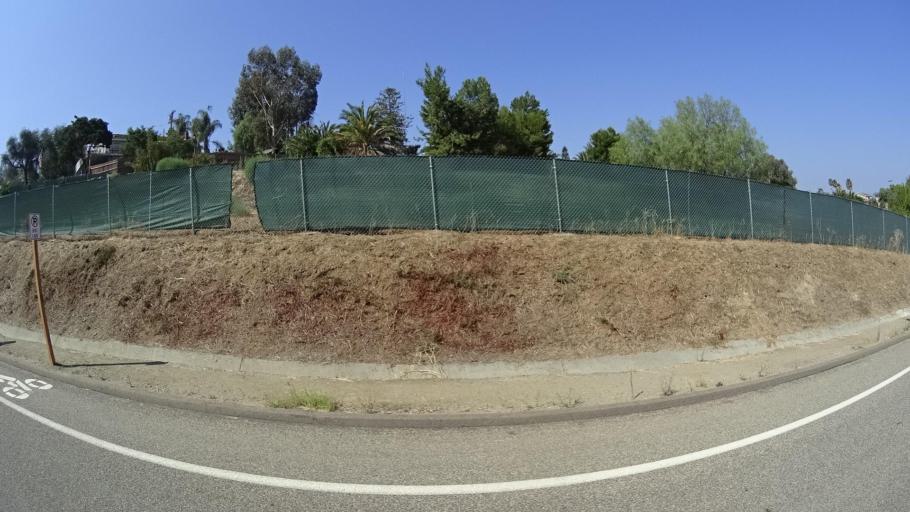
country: US
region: California
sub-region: San Diego County
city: Bonsall
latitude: 33.2495
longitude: -117.2298
